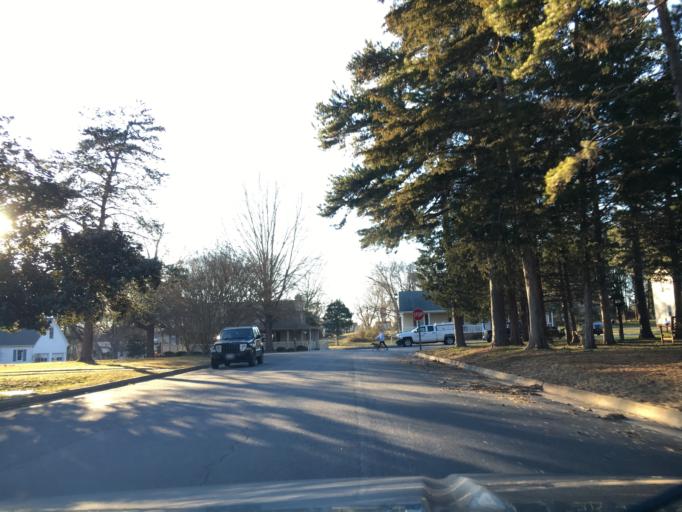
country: US
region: Virginia
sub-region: Halifax County
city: South Boston
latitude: 36.7061
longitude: -78.8841
